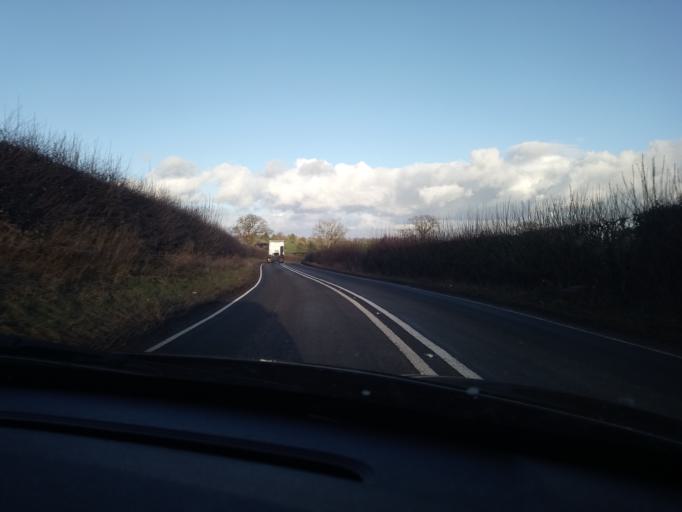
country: GB
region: England
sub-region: Shropshire
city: Ellesmere
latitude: 52.9052
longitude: -2.8517
